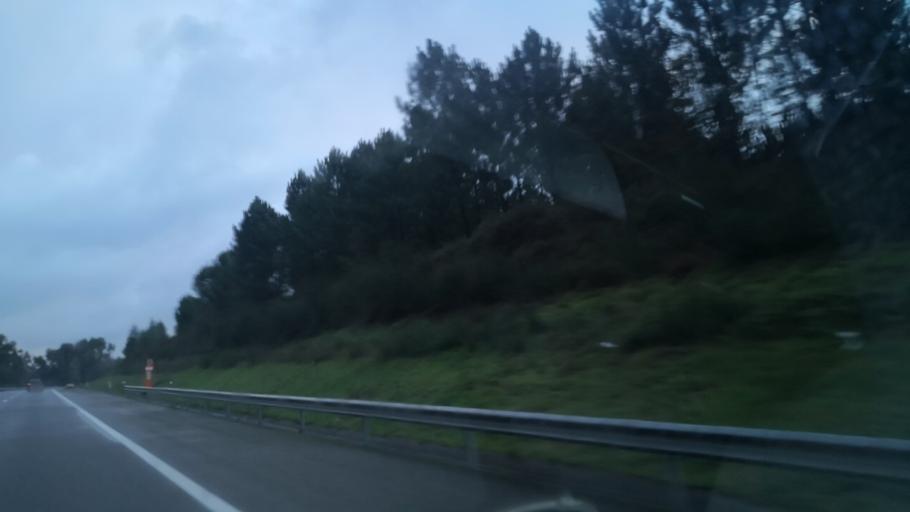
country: PT
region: Braga
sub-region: Vila Verde
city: Prado
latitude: 41.6629
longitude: -8.5483
